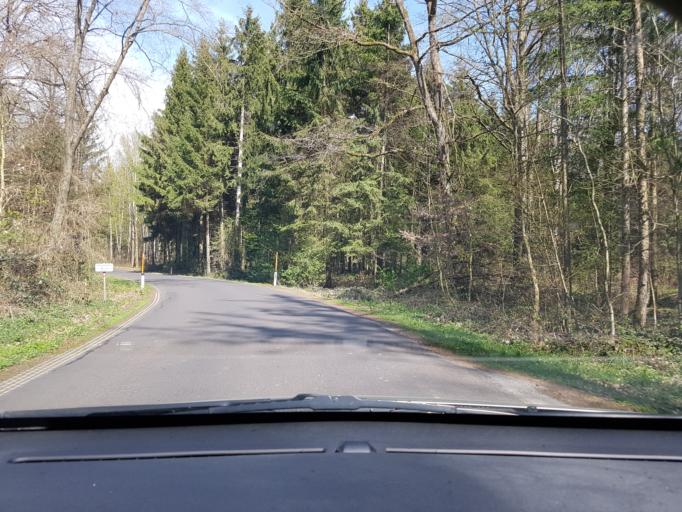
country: AT
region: Upper Austria
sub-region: Politischer Bezirk Linz-Land
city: Ansfelden
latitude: 48.1999
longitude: 14.3288
